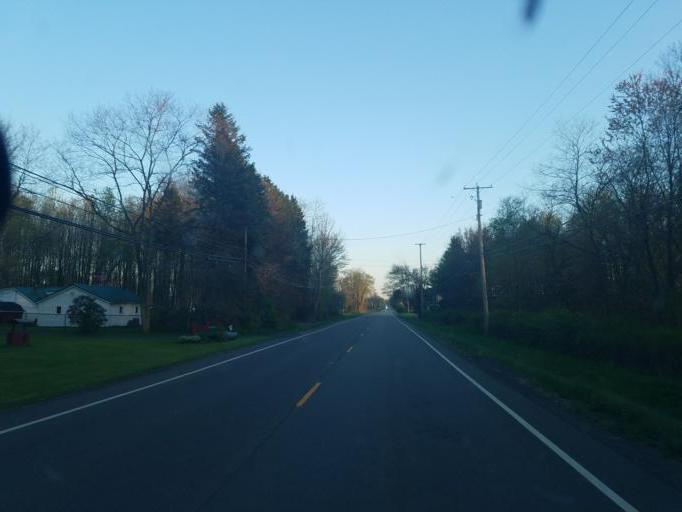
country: US
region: Ohio
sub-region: Trumbull County
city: Brookfield Center
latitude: 41.3261
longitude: -80.5682
